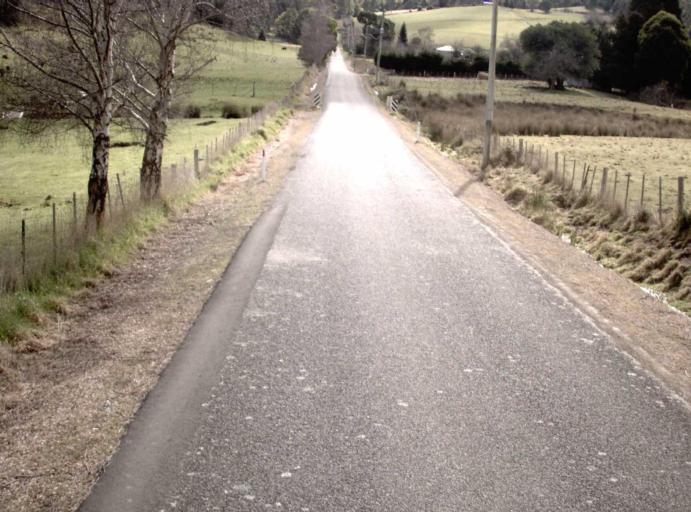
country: AU
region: Tasmania
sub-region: Launceston
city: Mayfield
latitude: -41.2519
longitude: 147.2452
